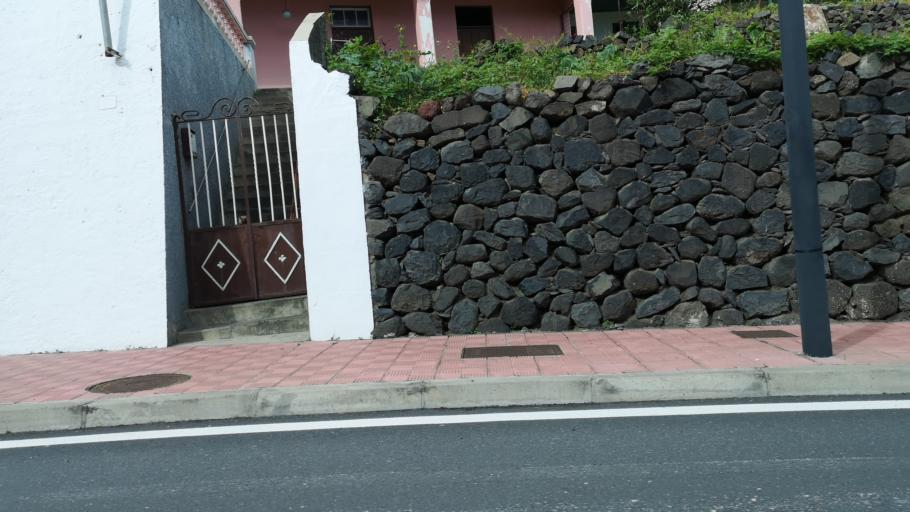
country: ES
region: Canary Islands
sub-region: Provincia de Santa Cruz de Tenerife
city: Hermigua
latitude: 28.1644
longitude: -17.1982
